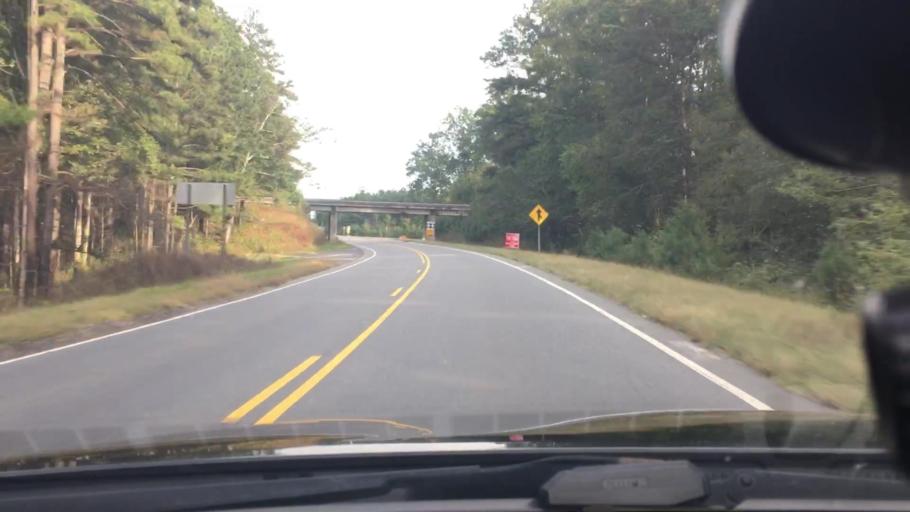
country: US
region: North Carolina
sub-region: Montgomery County
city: Troy
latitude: 35.3214
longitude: -79.9480
